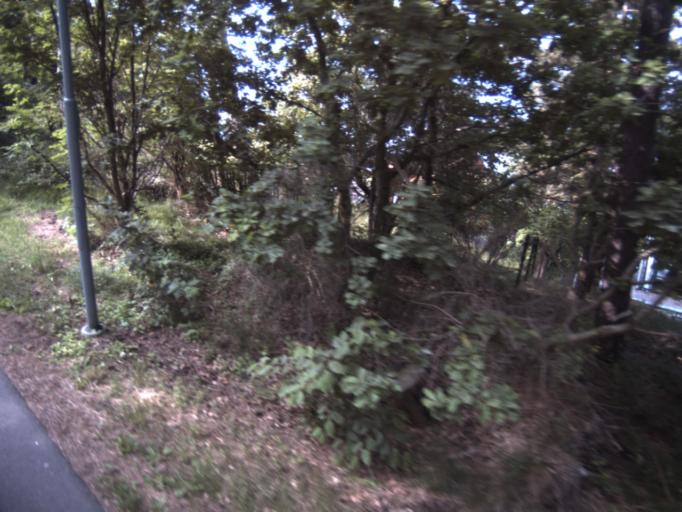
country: DK
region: Capital Region
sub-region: Helsingor Kommune
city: Helsingor
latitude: 56.0919
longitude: 12.6449
